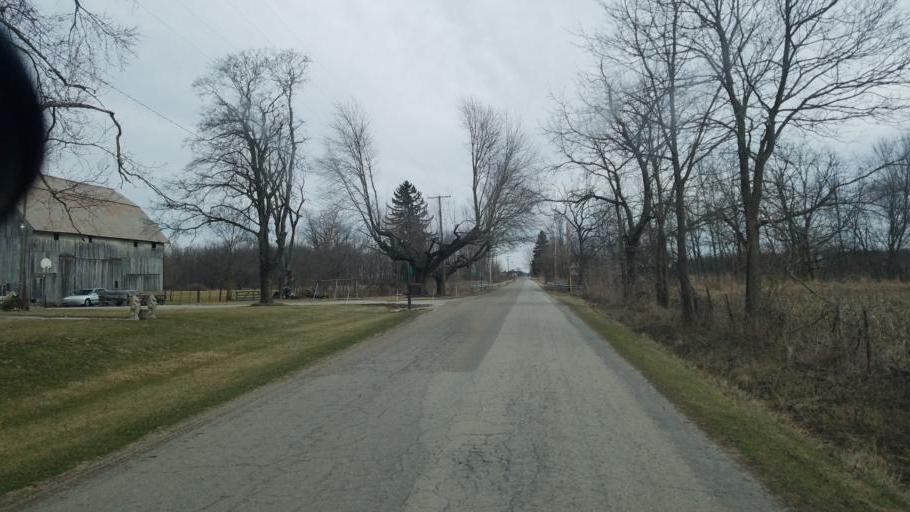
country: US
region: Ohio
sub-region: Delaware County
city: Ashley
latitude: 40.4559
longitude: -83.0067
